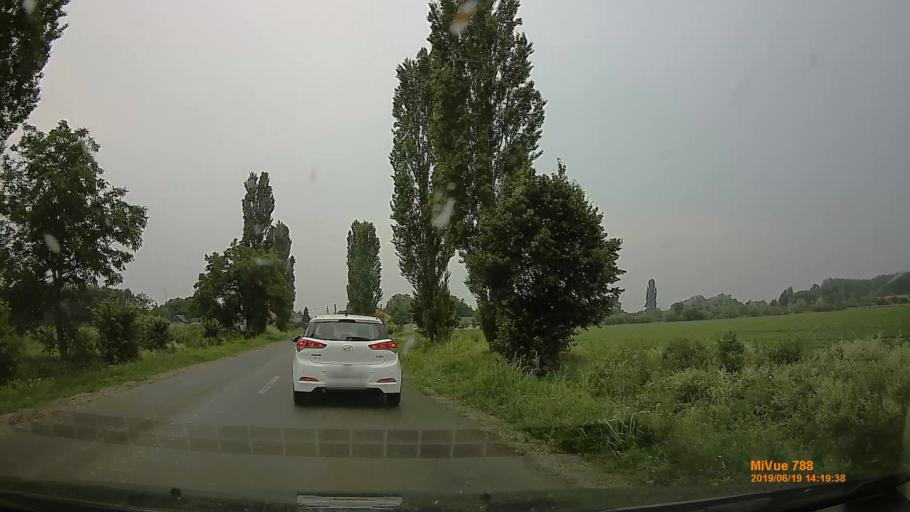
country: HU
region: Baranya
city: Szigetvar
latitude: 46.0305
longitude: 17.7796
